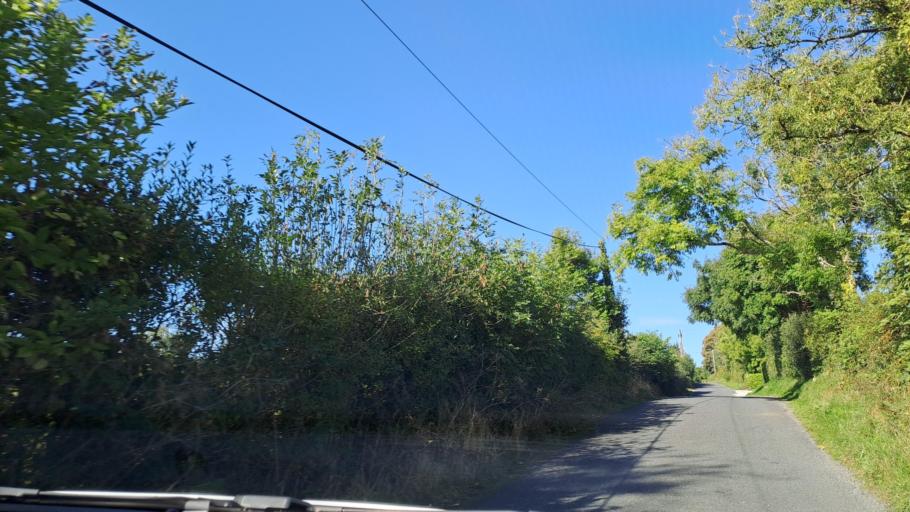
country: IE
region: Ulster
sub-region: County Monaghan
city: Carrickmacross
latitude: 53.9949
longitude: -6.7624
